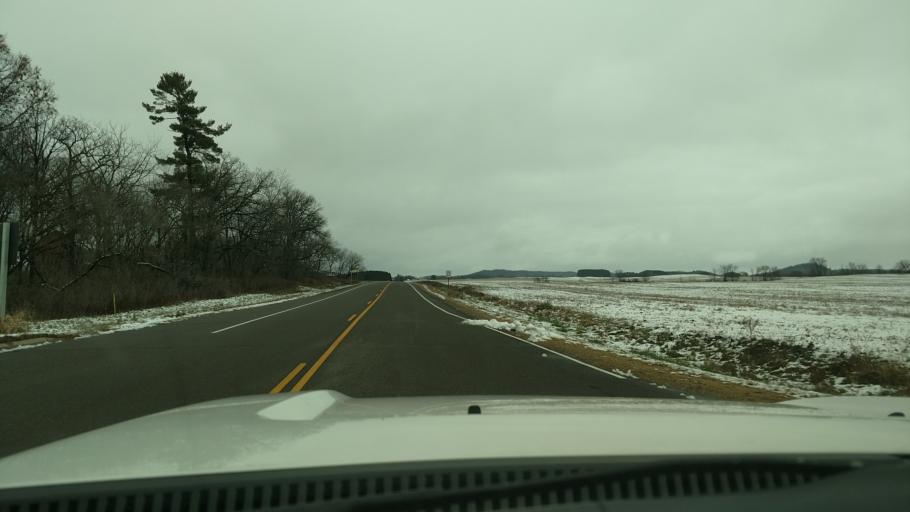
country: US
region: Wisconsin
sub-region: Dunn County
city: Colfax
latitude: 45.1427
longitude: -91.6872
